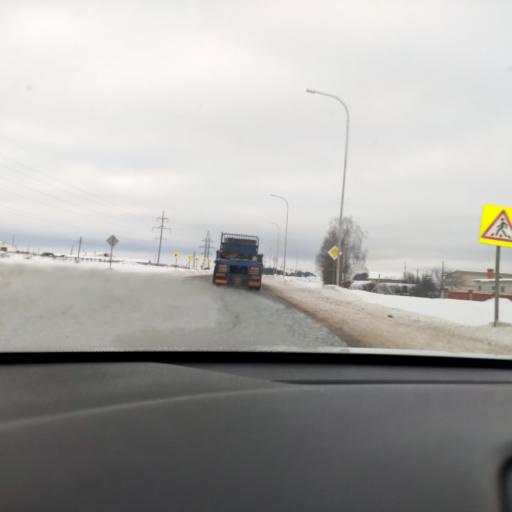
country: RU
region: Tatarstan
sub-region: Arskiy Rayon
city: Arsk
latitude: 56.1971
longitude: 49.9577
